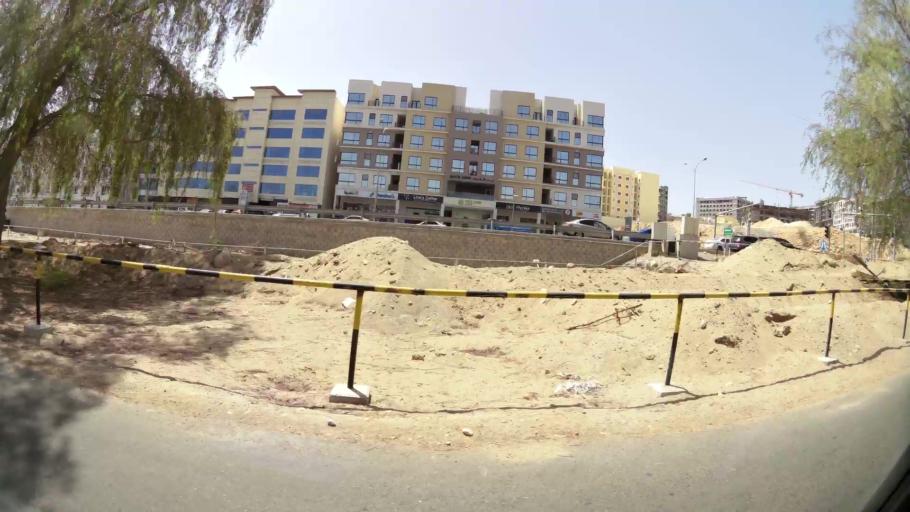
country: OM
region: Muhafazat Masqat
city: Muscat
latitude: 23.6206
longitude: 58.5028
